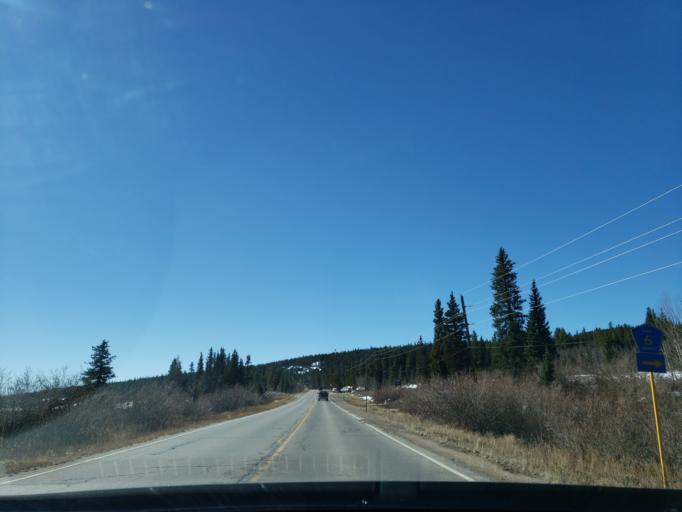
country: US
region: Colorado
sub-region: Park County
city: Fairplay
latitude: 39.2948
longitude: -106.0656
